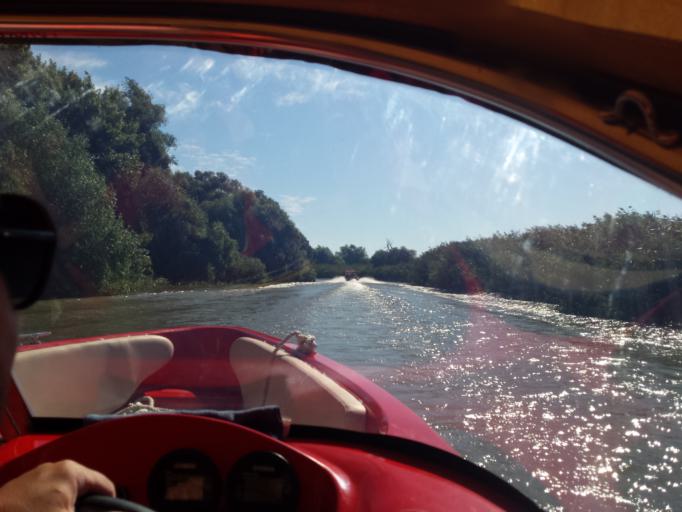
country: RO
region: Tulcea
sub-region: Comuna Pardina
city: Pardina
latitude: 45.2456
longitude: 29.0250
